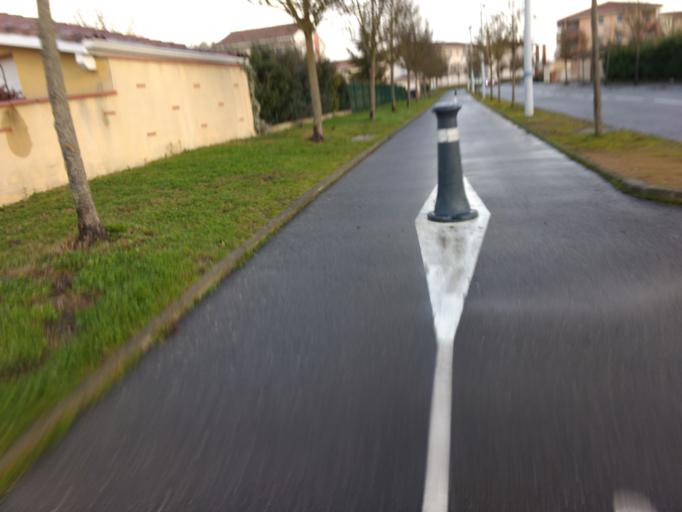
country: FR
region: Midi-Pyrenees
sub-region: Departement de la Haute-Garonne
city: Tournefeuille
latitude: 43.5986
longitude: 1.3222
